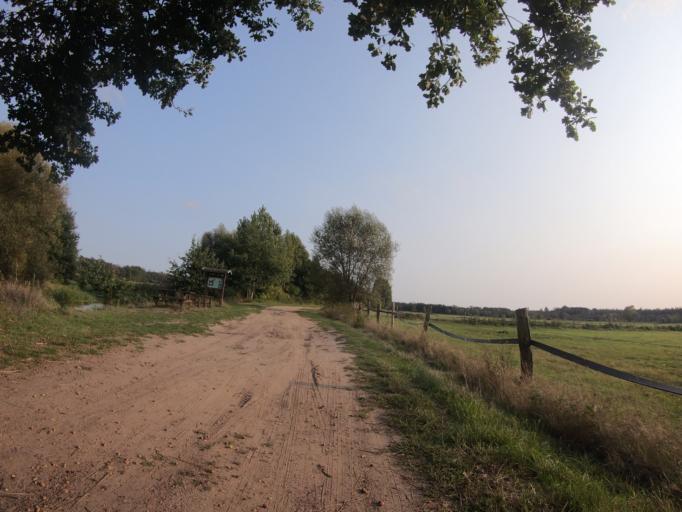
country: DE
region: Lower Saxony
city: Leiferde
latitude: 52.4779
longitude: 10.4650
